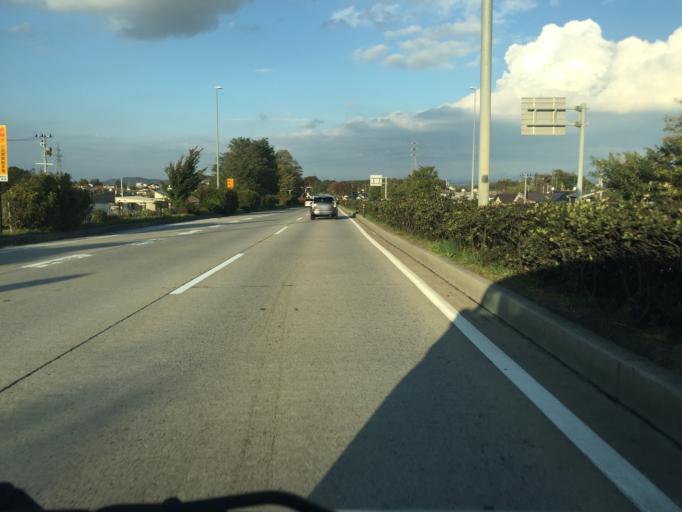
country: JP
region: Fukushima
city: Koriyama
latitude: 37.4284
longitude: 140.3622
